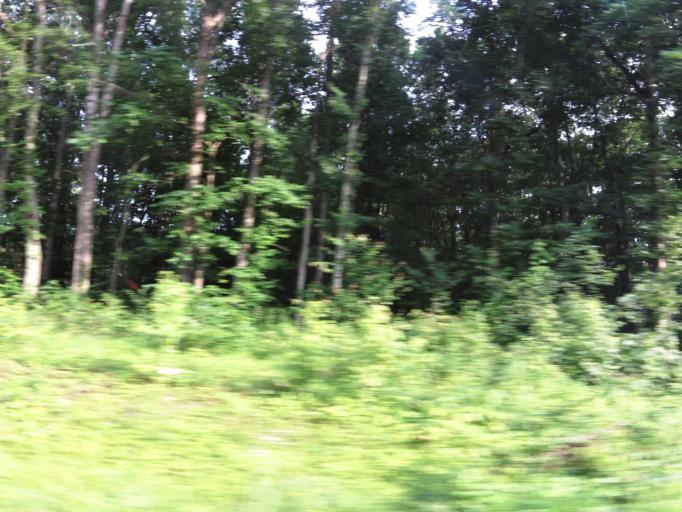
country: US
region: Tennessee
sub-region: Humphreys County
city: McEwen
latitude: 36.1031
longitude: -87.6593
